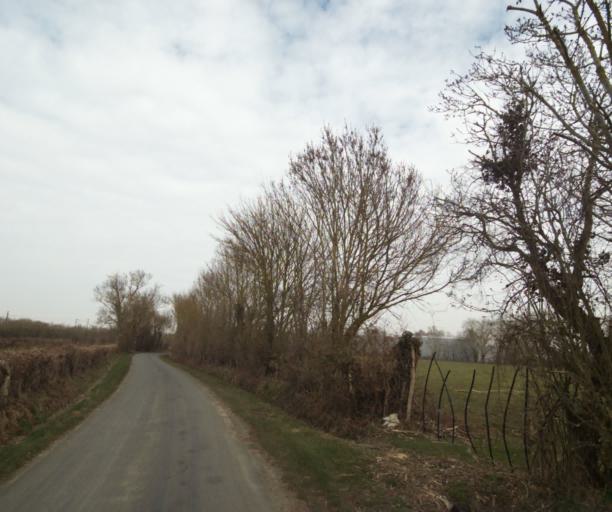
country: FR
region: Poitou-Charentes
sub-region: Departement des Deux-Sevres
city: Niort
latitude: 46.3000
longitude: -0.4679
